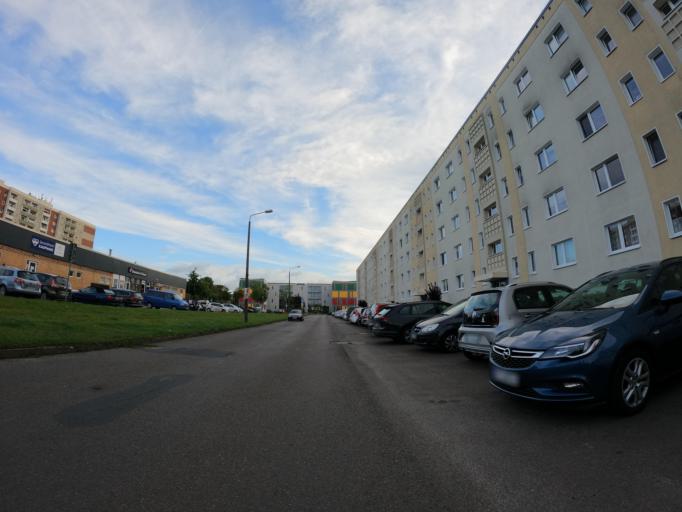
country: DE
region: Mecklenburg-Vorpommern
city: Kramerhof
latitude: 54.3247
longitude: 13.0540
